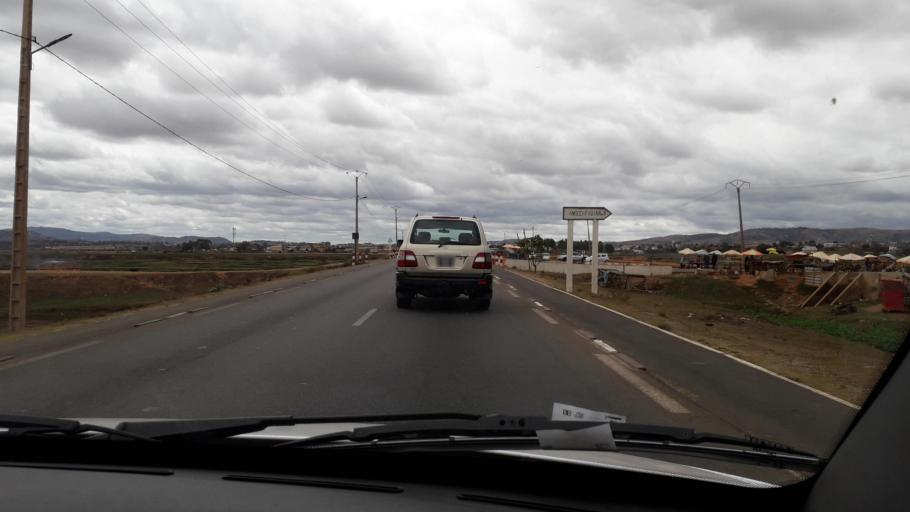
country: MG
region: Analamanga
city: Antananarivo
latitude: -18.8183
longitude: 47.5160
